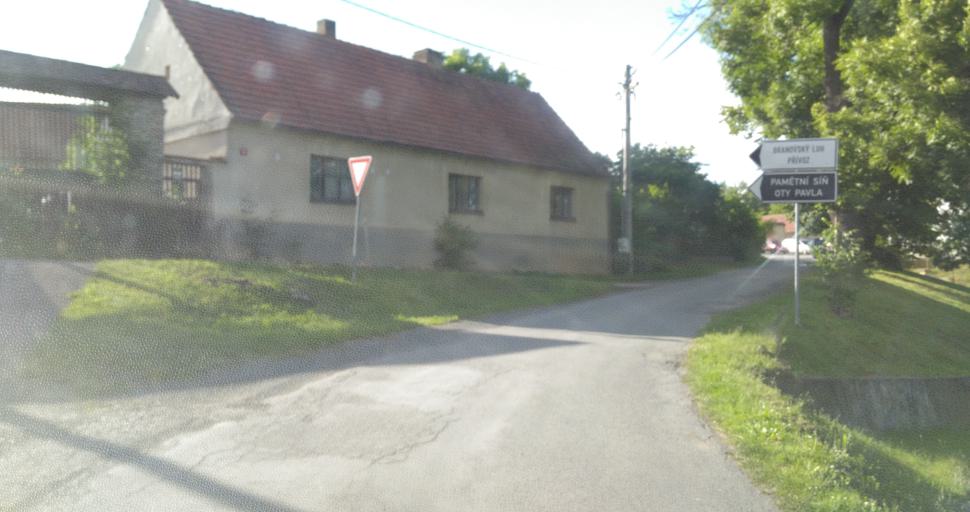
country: CZ
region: Central Bohemia
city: Roztoky
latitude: 50.0131
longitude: 13.8424
